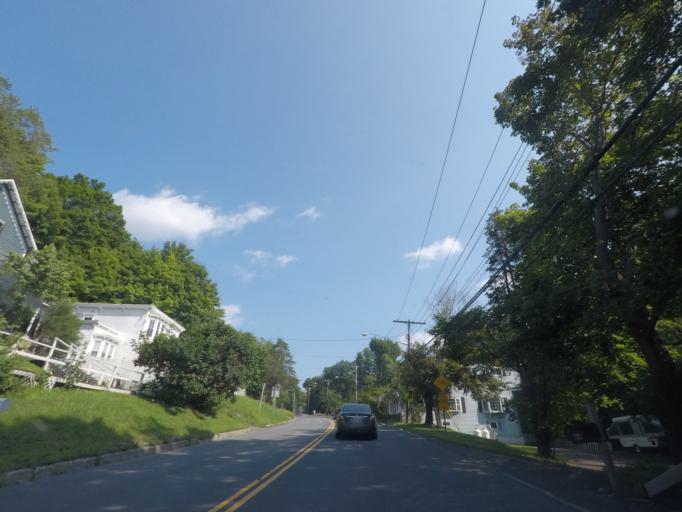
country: US
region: New York
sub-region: Rensselaer County
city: Nassau
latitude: 42.5133
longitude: -73.6053
